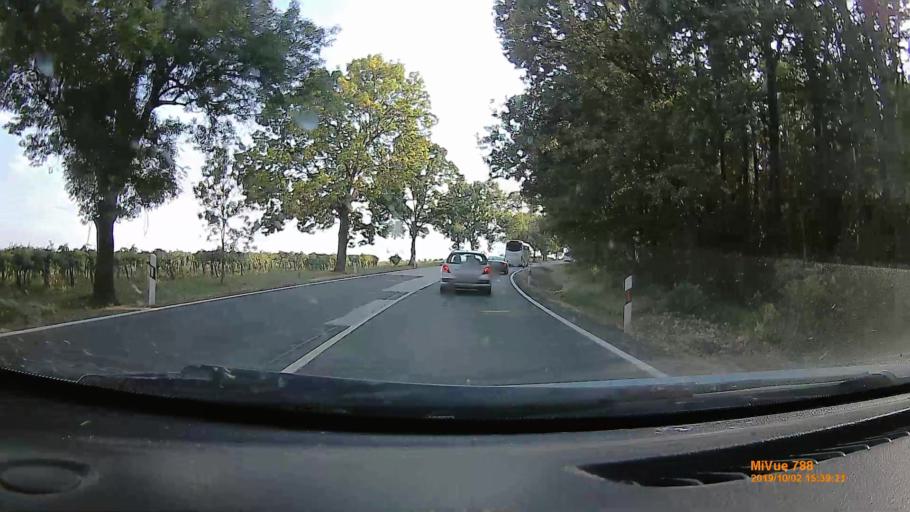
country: HU
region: Heves
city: Kerecsend
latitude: 47.8177
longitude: 20.3586
